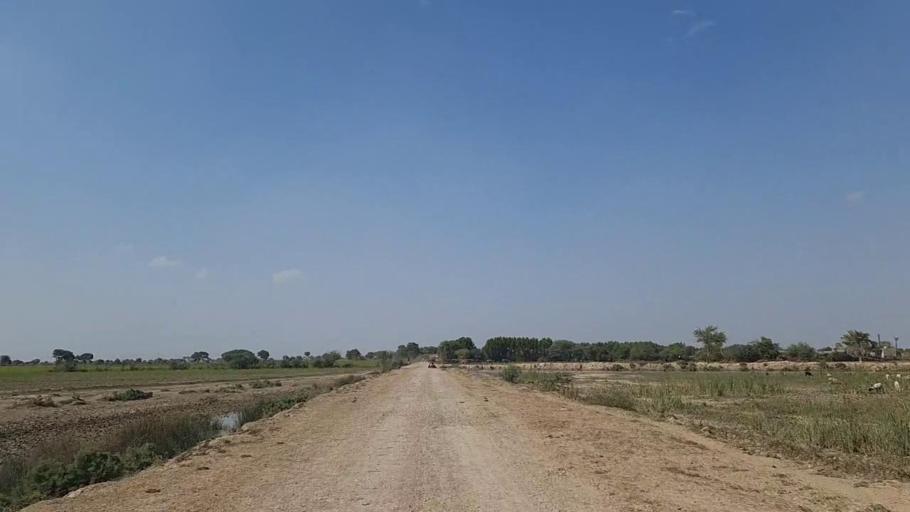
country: PK
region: Sindh
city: Jati
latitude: 24.5174
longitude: 68.2941
